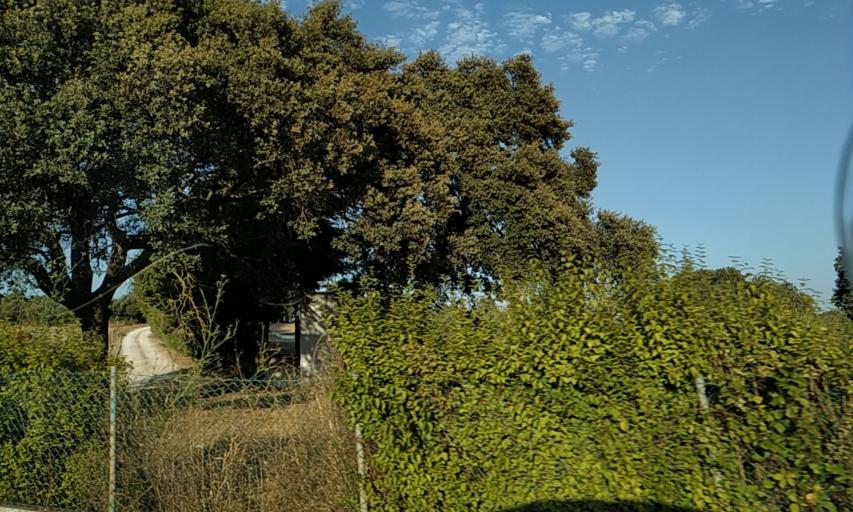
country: PT
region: Santarem
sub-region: Alcanena
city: Alcanena
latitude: 39.4416
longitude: -8.6247
